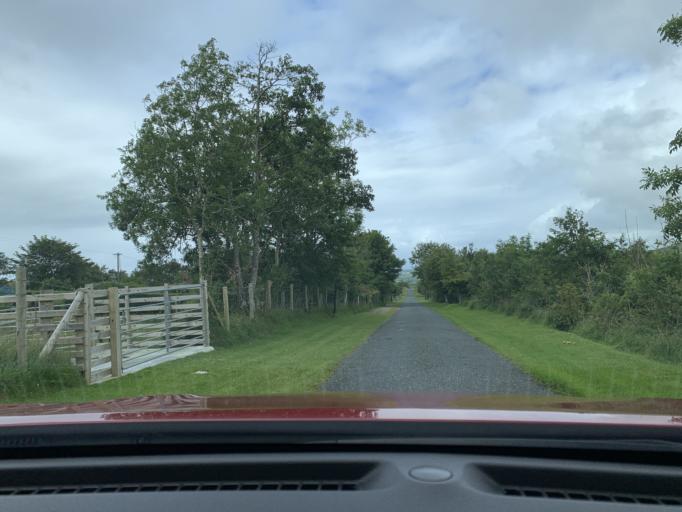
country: IE
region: Connaught
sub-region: County Leitrim
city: Kinlough
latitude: 54.3908
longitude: -8.4056
